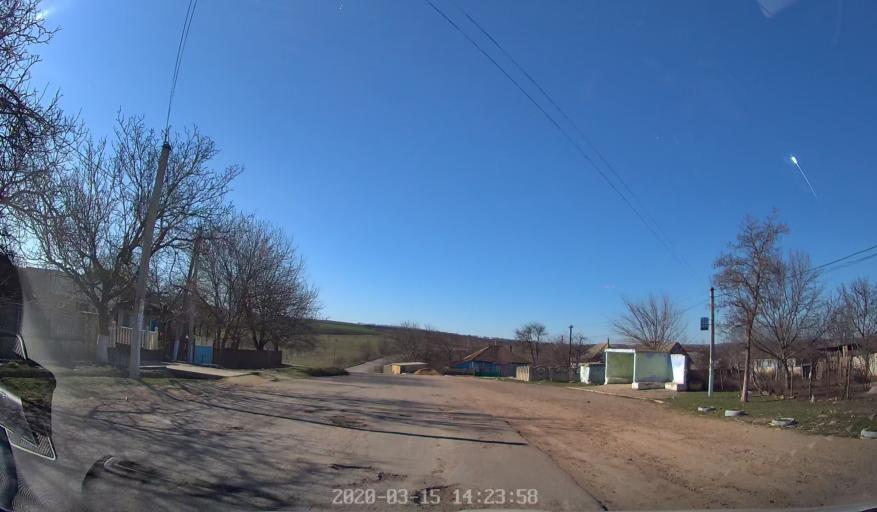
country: MD
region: Orhei
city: Orhei
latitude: 47.3318
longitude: 28.9210
